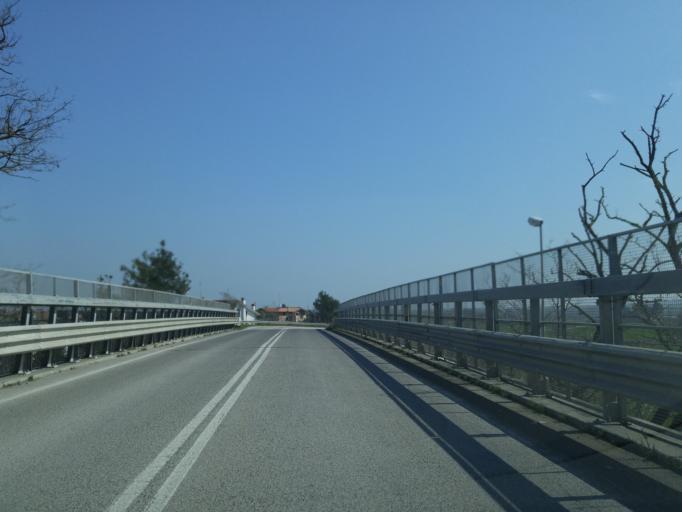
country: IT
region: The Marches
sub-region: Provincia di Pesaro e Urbino
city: Rosciano
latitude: 43.8124
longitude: 13.0181
